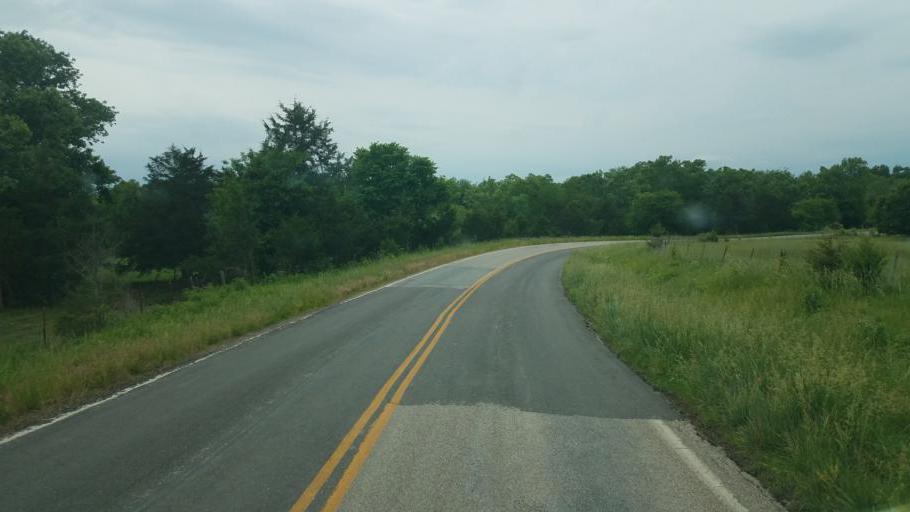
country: US
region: Missouri
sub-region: Moniteau County
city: California
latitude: 38.6847
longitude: -92.6098
